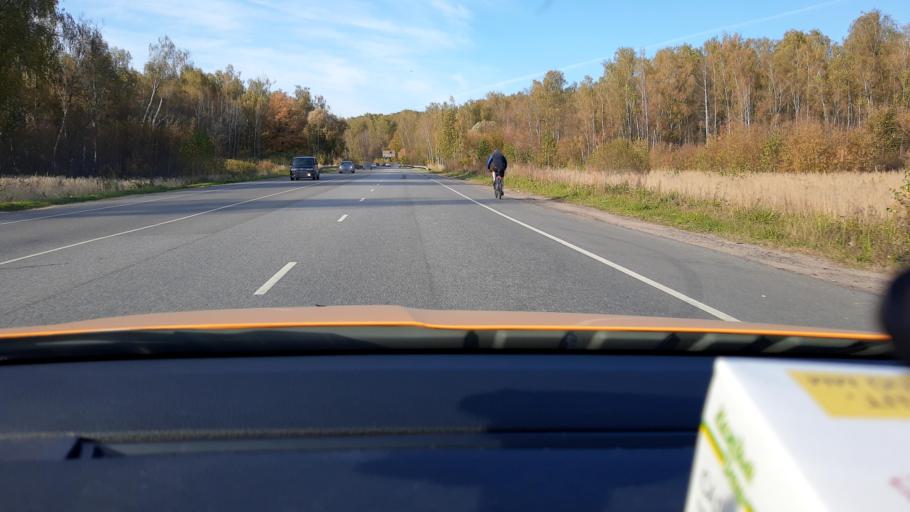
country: RU
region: Moskovskaya
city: Gorki-Leninskiye
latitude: 55.5255
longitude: 37.7891
